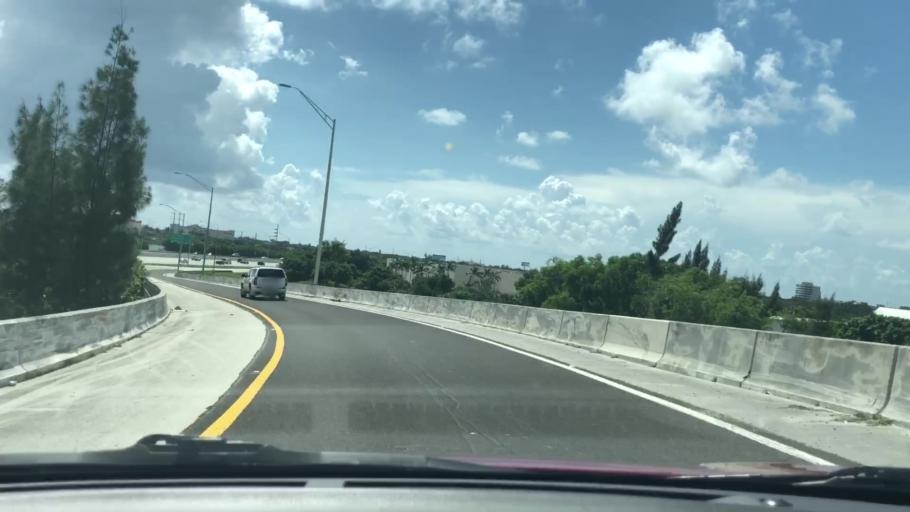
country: US
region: Florida
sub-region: Palm Beach County
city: West Palm Beach
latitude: 26.7054
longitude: -80.0771
